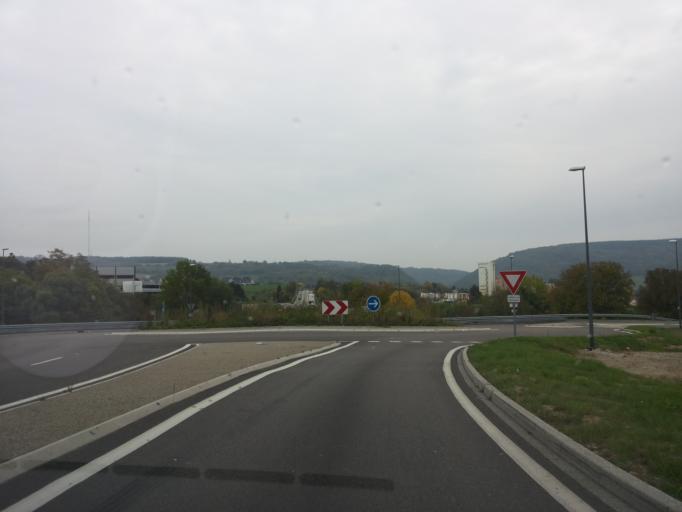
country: FR
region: Alsace
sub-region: Departement du Bas-Rhin
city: Wasselonne
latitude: 48.6447
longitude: 7.4422
